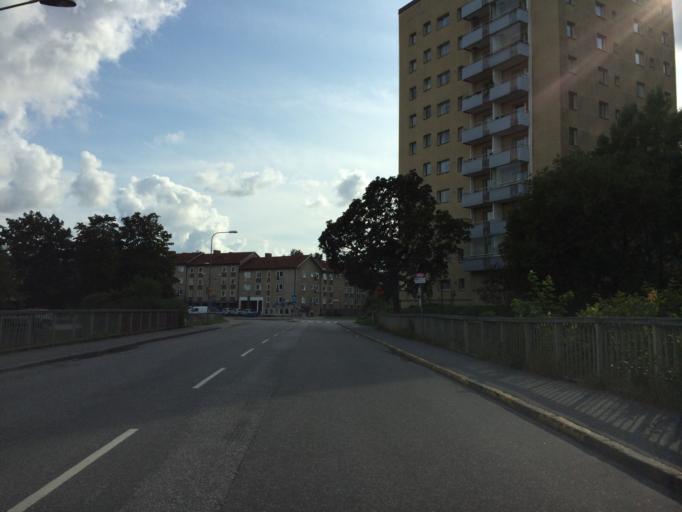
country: SE
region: Stockholm
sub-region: Huddinge Kommun
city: Segeltorp
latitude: 59.2859
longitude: 17.9629
